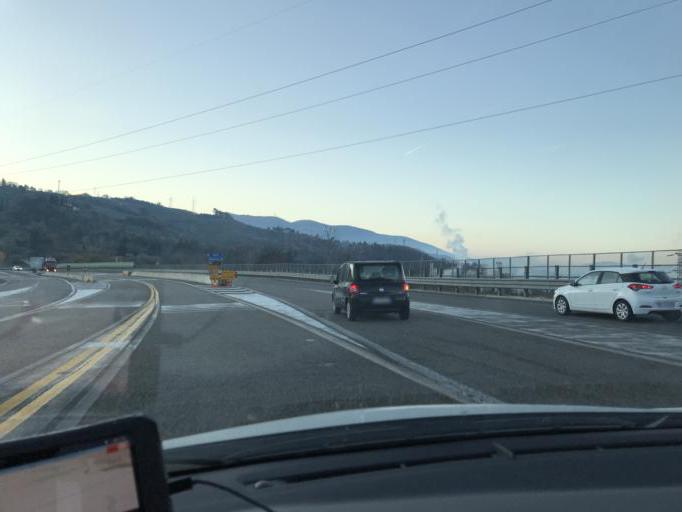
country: IT
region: Umbria
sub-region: Provincia di Terni
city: Terni
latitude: 42.5773
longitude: 12.6802
